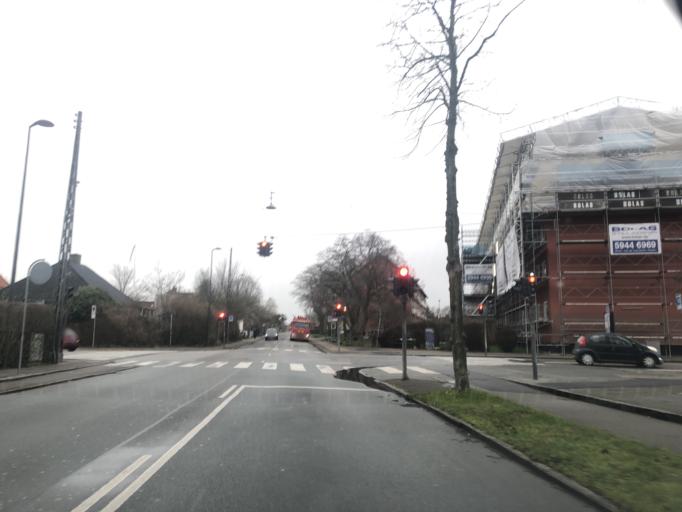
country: DK
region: Capital Region
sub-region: Tarnby Kommune
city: Tarnby
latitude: 55.6463
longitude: 12.6053
